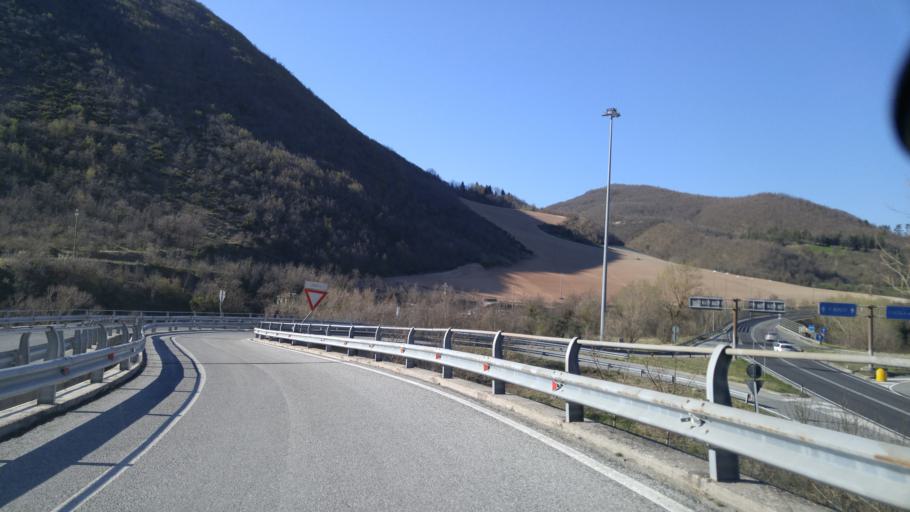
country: IT
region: The Marches
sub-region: Provincia di Pesaro e Urbino
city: Cagli
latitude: 43.5431
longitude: 12.6398
